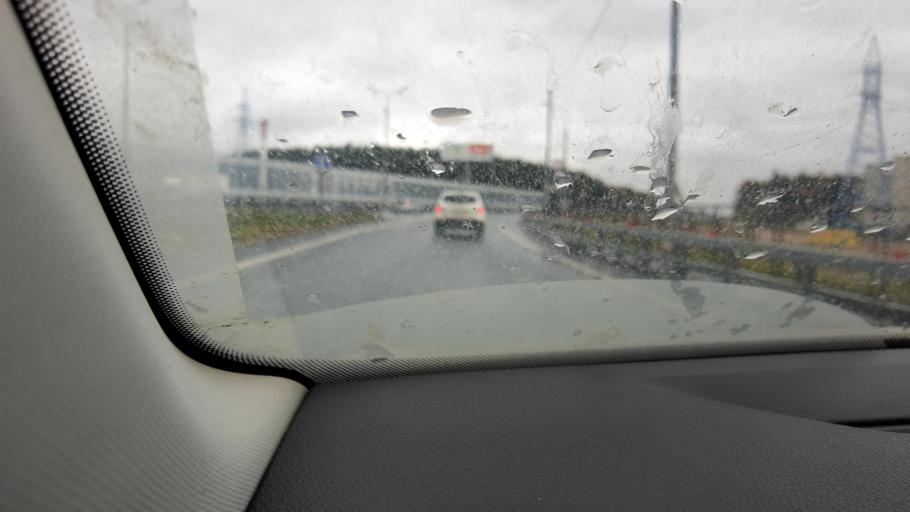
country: RU
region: Moskovskaya
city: Aprelevka
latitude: 55.5392
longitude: 37.0841
